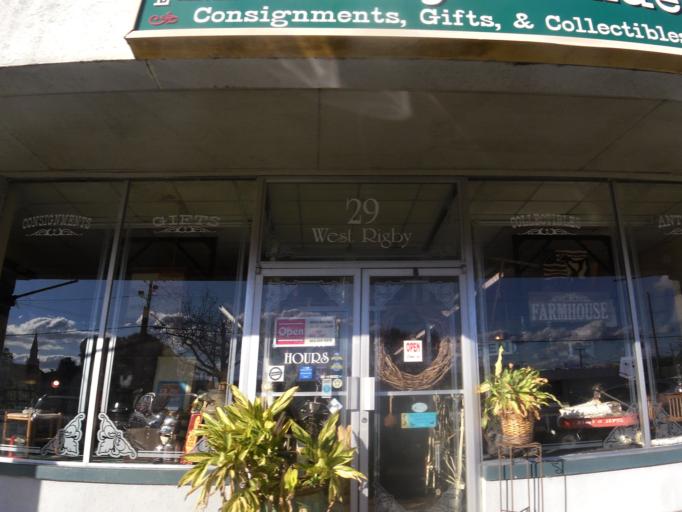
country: US
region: South Carolina
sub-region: Clarendon County
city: Manning
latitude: 33.6969
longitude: -80.2117
